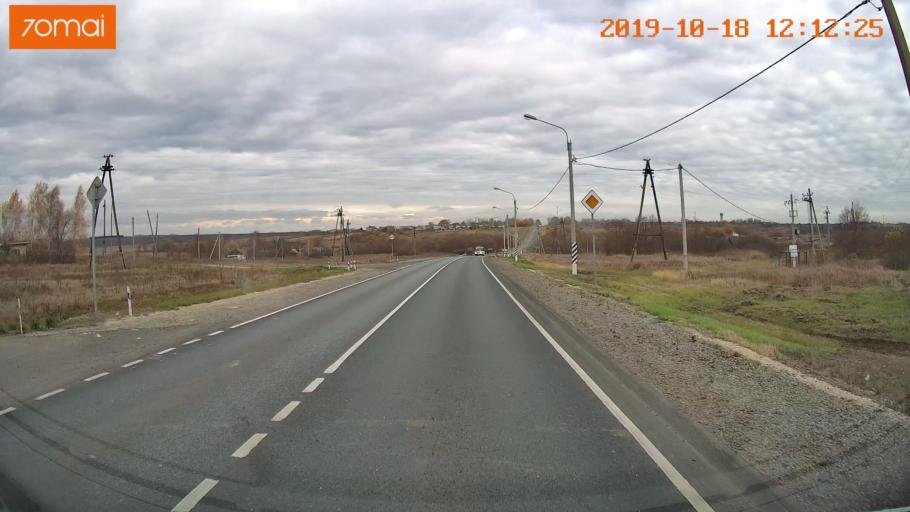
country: RU
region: Rjazan
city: Zakharovo
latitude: 54.4115
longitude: 39.3579
